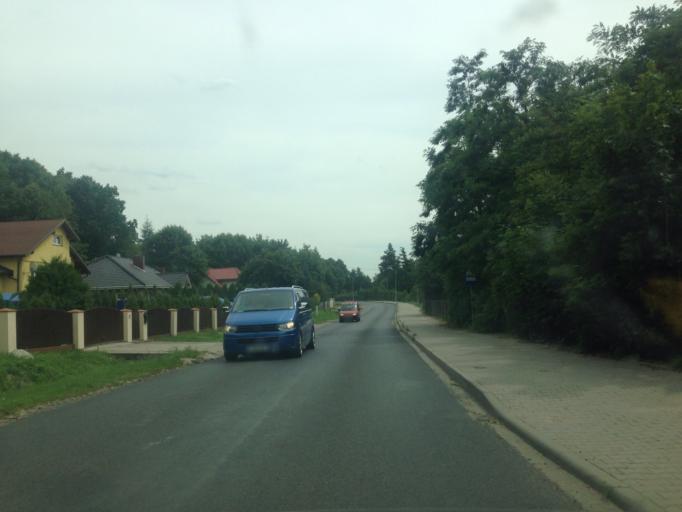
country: PL
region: Kujawsko-Pomorskie
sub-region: Powiat brodnicki
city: Brodnica
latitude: 53.2755
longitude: 19.3887
